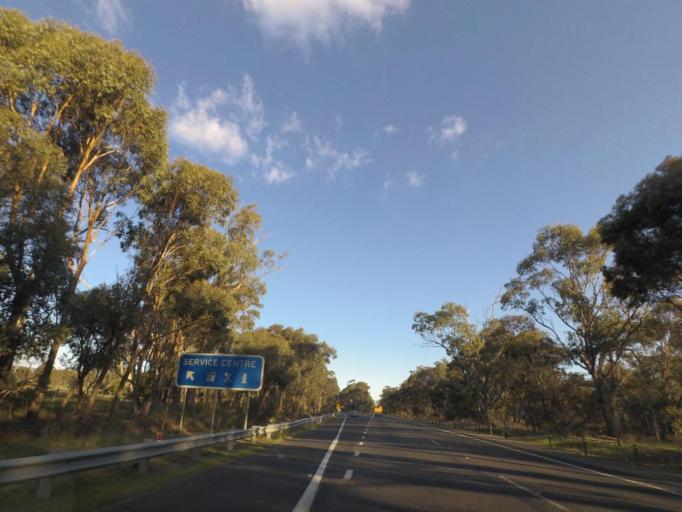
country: AU
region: Victoria
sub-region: Murrindindi
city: Kinglake West
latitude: -37.0597
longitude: 145.1010
